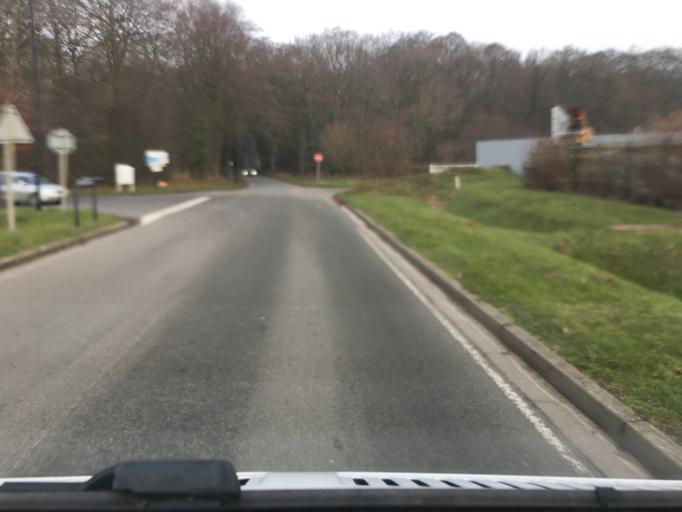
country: FR
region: Picardie
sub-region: Departement de la Somme
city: Saint-Valery-sur-Somme
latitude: 50.1740
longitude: 1.6362
